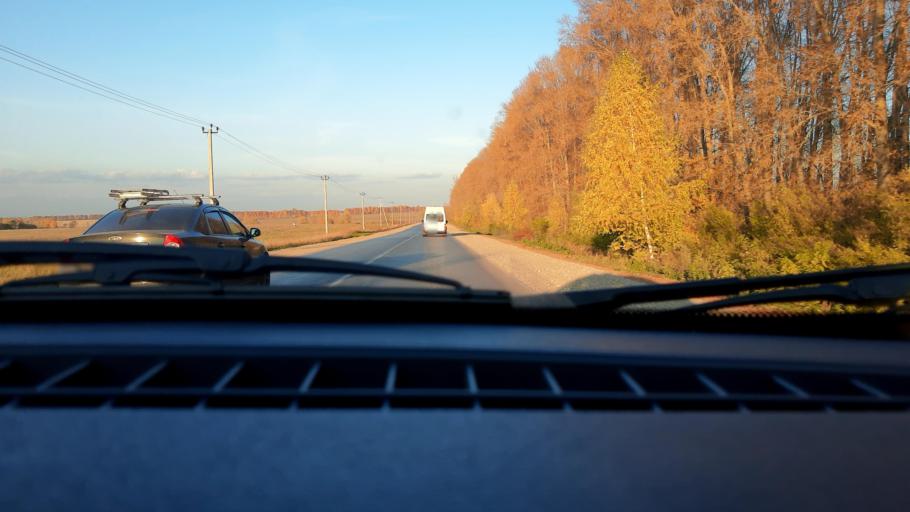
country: RU
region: Bashkortostan
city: Asanovo
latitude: 54.8199
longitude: 55.6094
